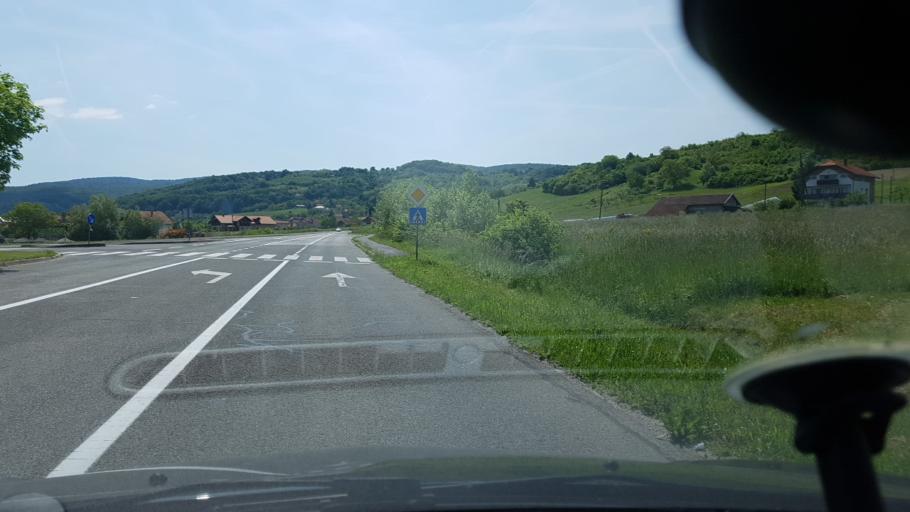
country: HR
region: Krapinsko-Zagorska
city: Marija Bistrica
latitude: 46.0004
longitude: 16.1155
